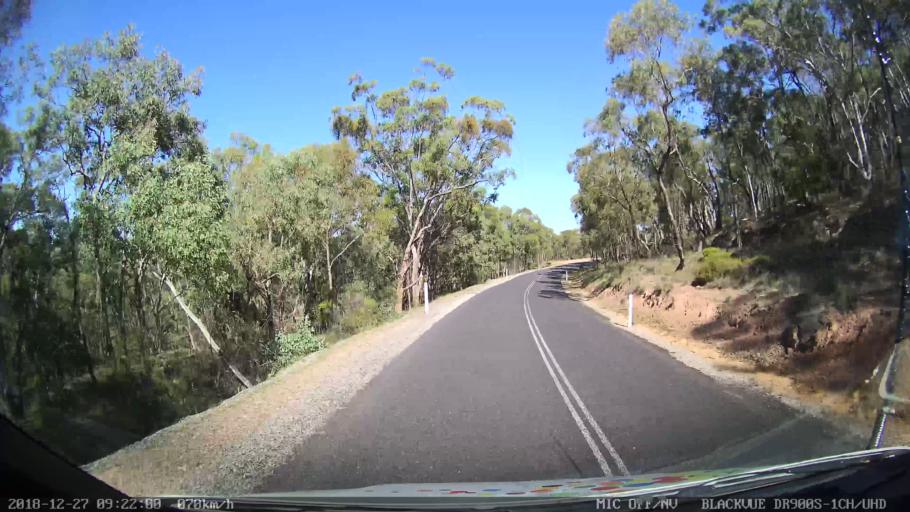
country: AU
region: New South Wales
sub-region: Lithgow
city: Portland
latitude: -33.1282
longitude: 150.0127
